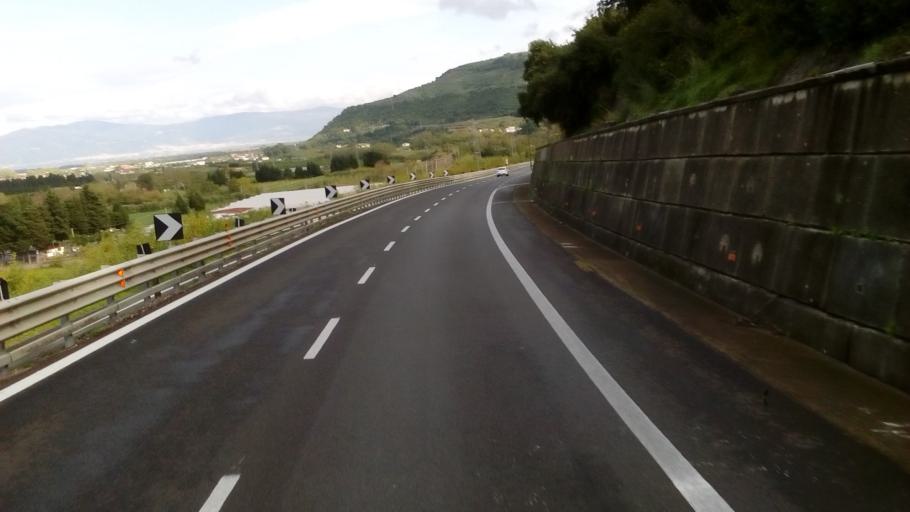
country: IT
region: Calabria
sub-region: Provincia di Vibo-Valentia
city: Pizzo
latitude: 38.7678
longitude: 16.2071
